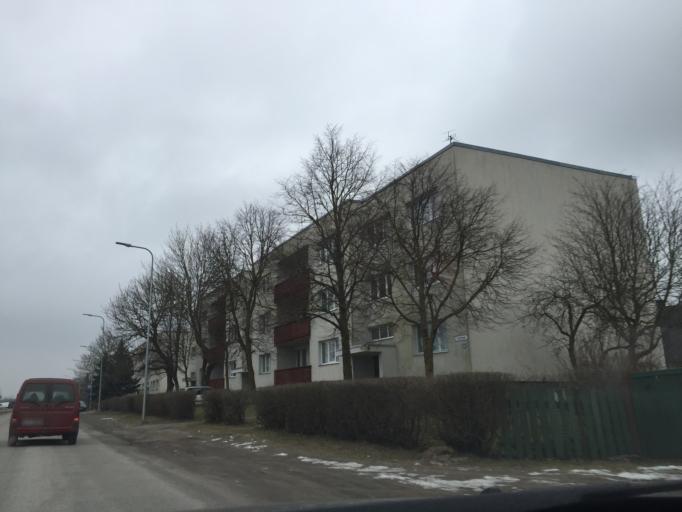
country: EE
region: Saare
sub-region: Kuressaare linn
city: Kuressaare
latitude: 58.2575
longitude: 22.4787
